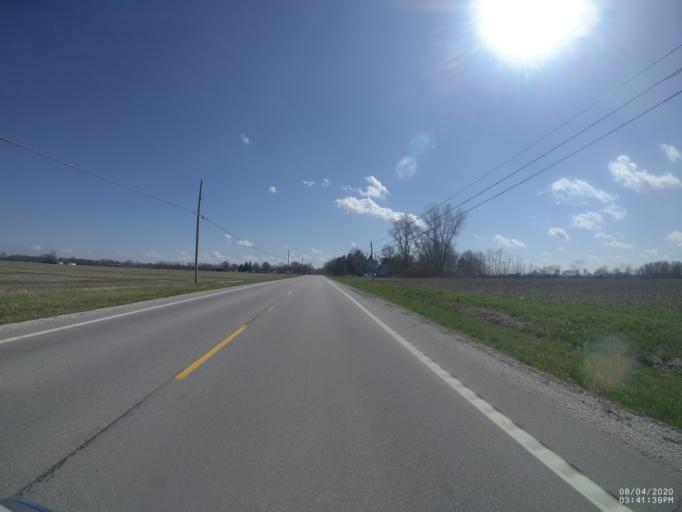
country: US
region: Ohio
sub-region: Sandusky County
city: Stony Prairie
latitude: 41.2582
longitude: -83.2356
